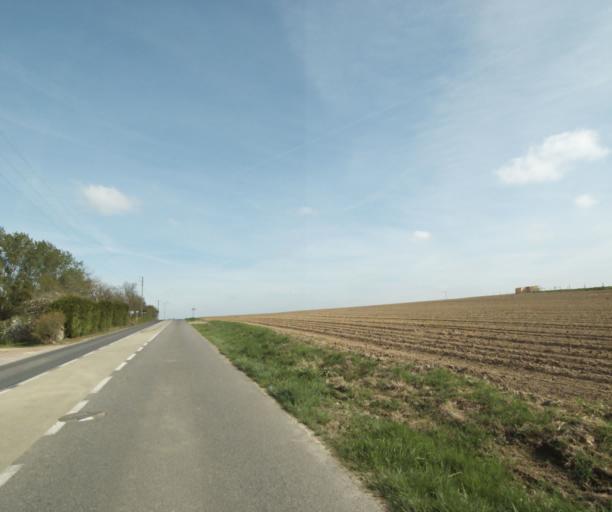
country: FR
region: Ile-de-France
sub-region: Departement de Seine-et-Marne
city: Nangis
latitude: 48.5654
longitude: 3.0129
